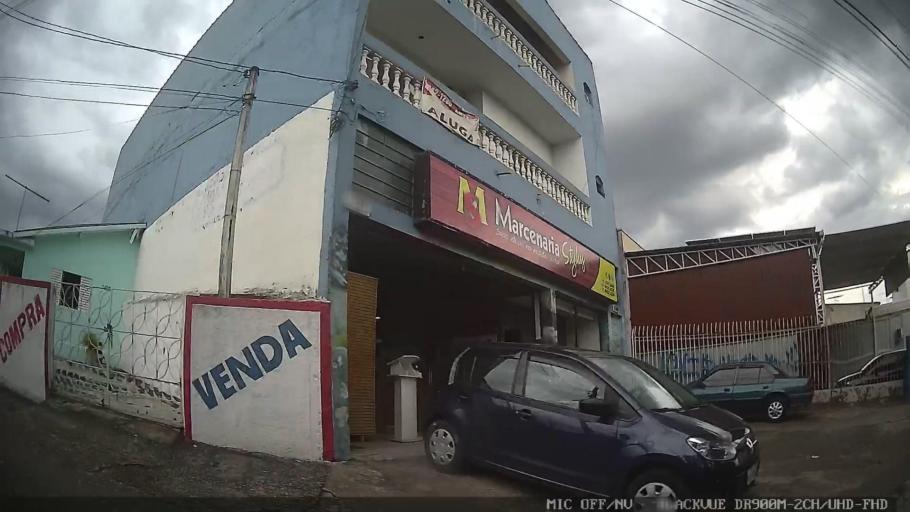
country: BR
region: Sao Paulo
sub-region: Suzano
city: Suzano
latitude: -23.5544
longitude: -46.3112
